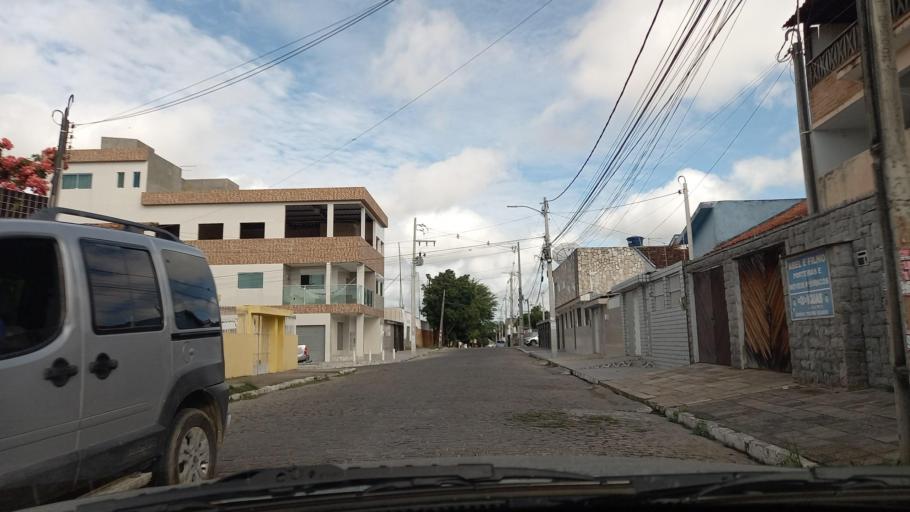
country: BR
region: Pernambuco
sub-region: Caruaru
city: Caruaru
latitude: -8.2901
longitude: -35.9795
